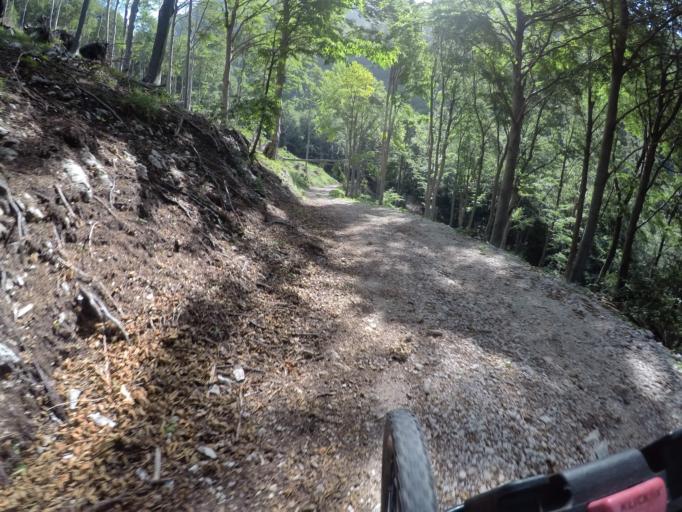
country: IT
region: Friuli Venezia Giulia
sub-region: Provincia di Udine
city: Resiutta
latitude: 46.3336
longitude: 13.2174
